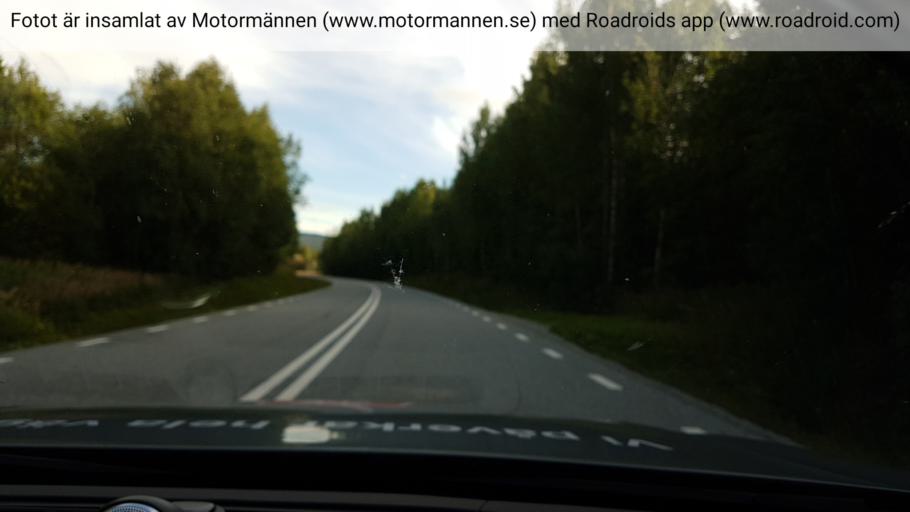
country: SE
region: Jaemtland
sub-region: Stroemsunds Kommun
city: Stroemsund
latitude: 64.1581
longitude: 15.6745
